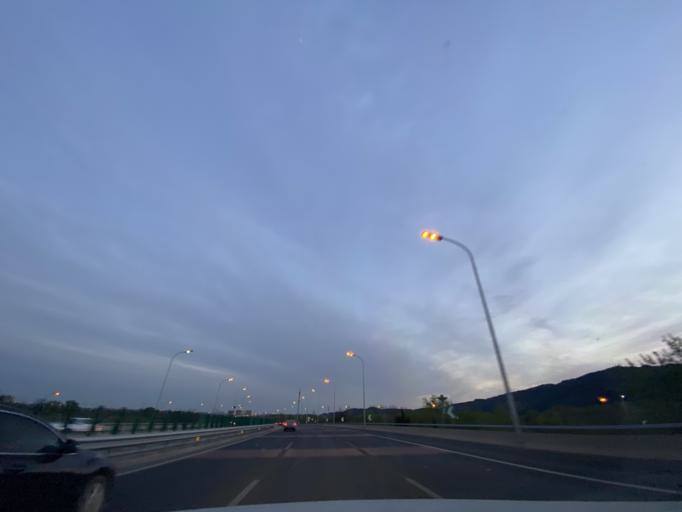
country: CN
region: Beijing
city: Xiangshan
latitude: 39.9903
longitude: 116.2155
